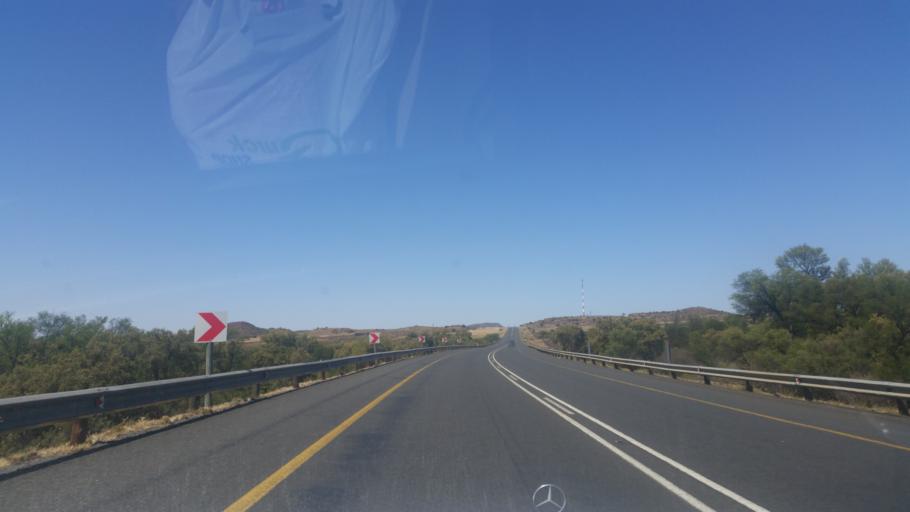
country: ZA
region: Northern Cape
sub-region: Pixley ka Seme District Municipality
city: Colesberg
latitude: -30.6162
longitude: 25.2928
